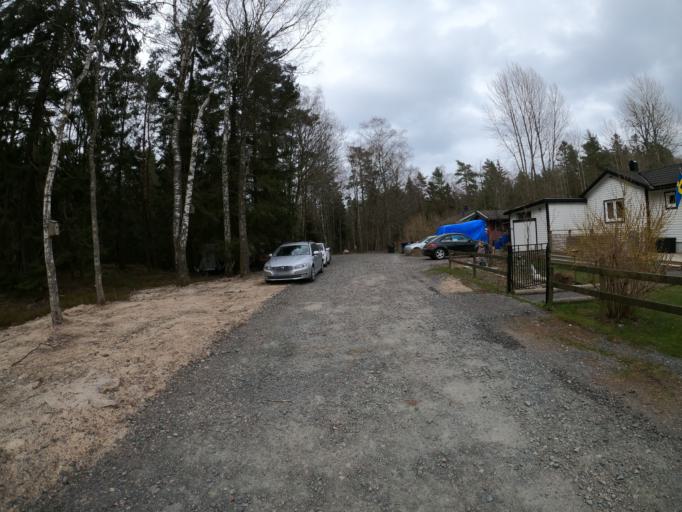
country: SE
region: Vaestra Goetaland
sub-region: Harryda Kommun
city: Molnlycke
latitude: 57.6208
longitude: 12.1038
